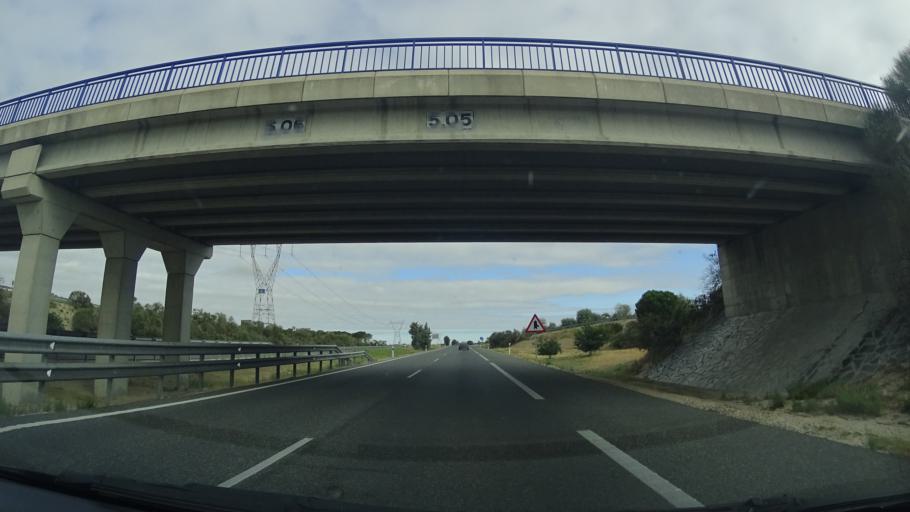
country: ES
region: Castille and Leon
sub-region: Provincia de Valladolid
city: San Pablo de la Moraleja
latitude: 41.1492
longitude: -4.7887
